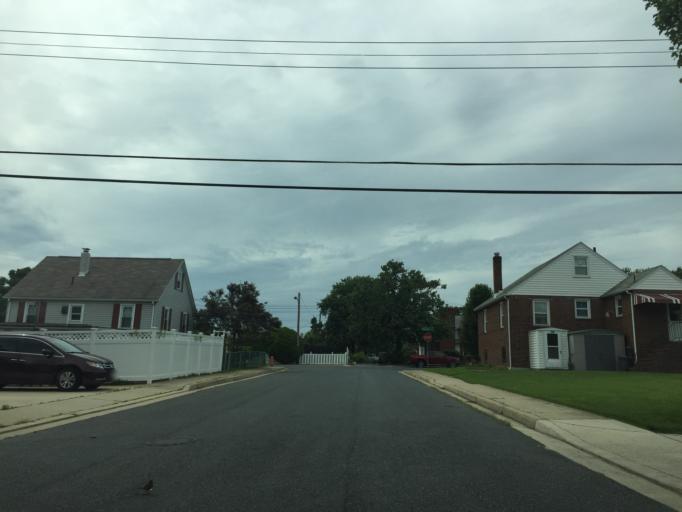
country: US
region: Maryland
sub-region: Baltimore County
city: Edgemere
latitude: 39.2401
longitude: -76.4542
